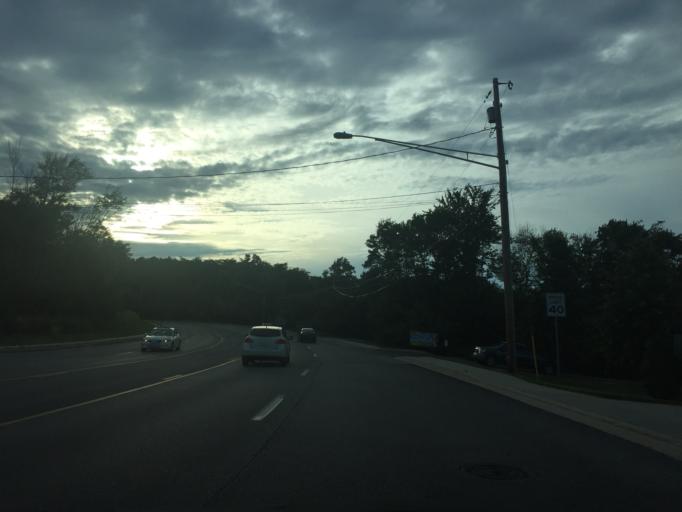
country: US
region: Maryland
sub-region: Baltimore County
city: Rossville
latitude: 39.3570
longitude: -76.4872
